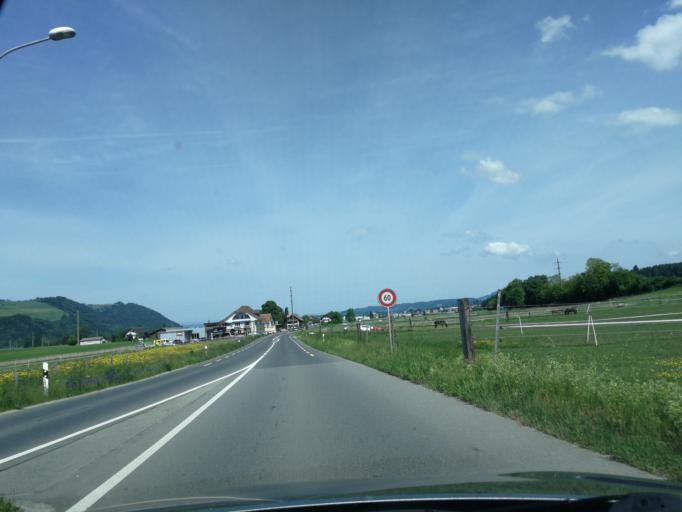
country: CH
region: Bern
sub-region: Bern-Mittelland District
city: Niederwichtrach
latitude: 46.8525
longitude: 7.5739
